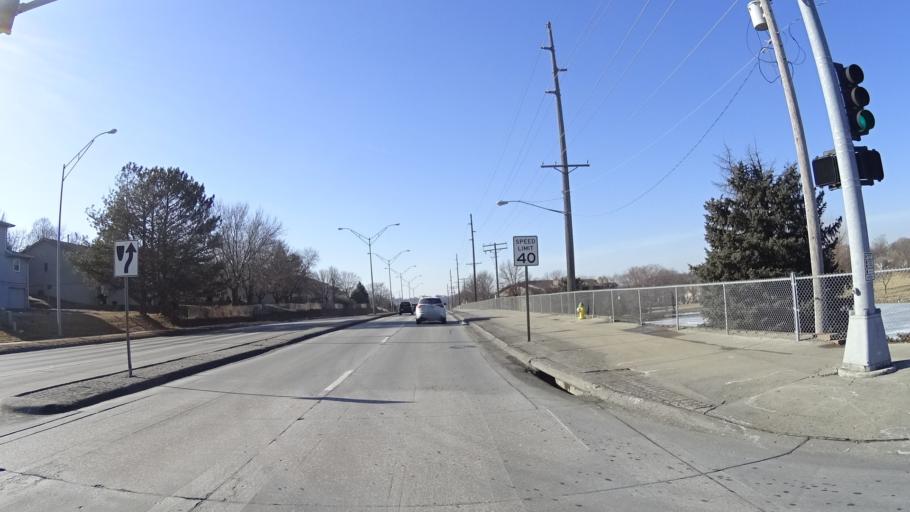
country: US
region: Nebraska
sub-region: Douglas County
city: Bennington
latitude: 41.3067
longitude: -96.0893
